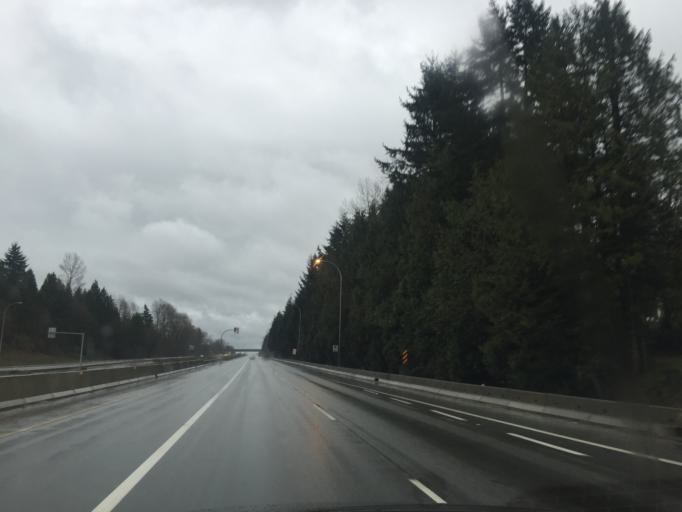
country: CA
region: British Columbia
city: Walnut Grove
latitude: 49.1611
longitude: -122.6581
